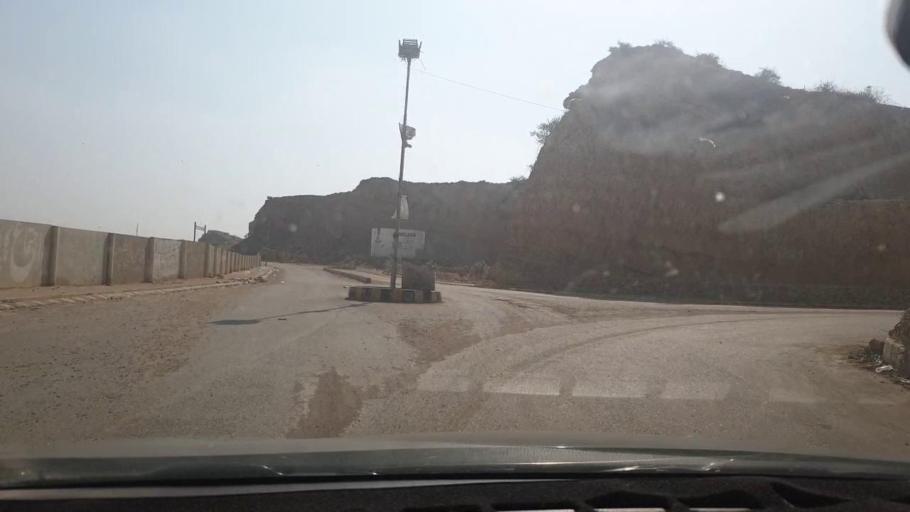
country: PK
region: Sindh
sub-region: Karachi District
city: Karachi
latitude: 24.9685
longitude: 66.9979
